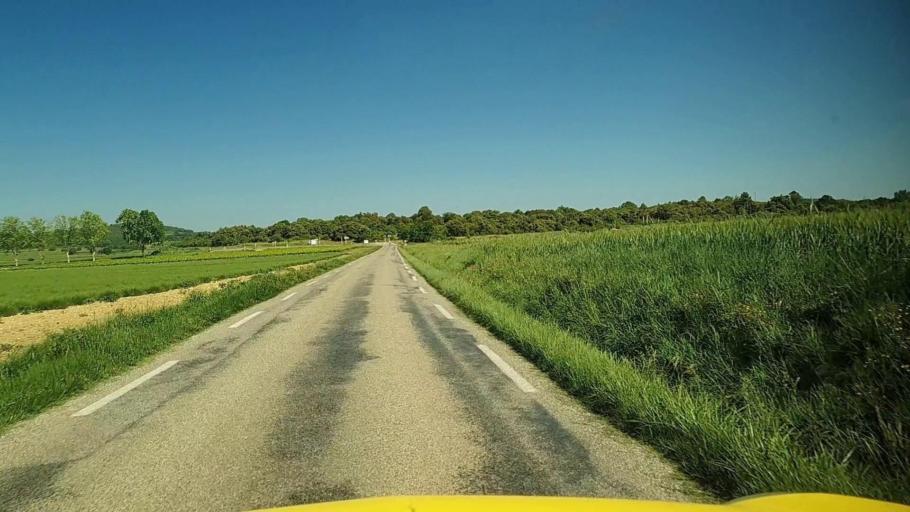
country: FR
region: Languedoc-Roussillon
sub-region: Departement du Gard
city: Saint-Chaptes
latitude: 43.9832
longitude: 4.2740
